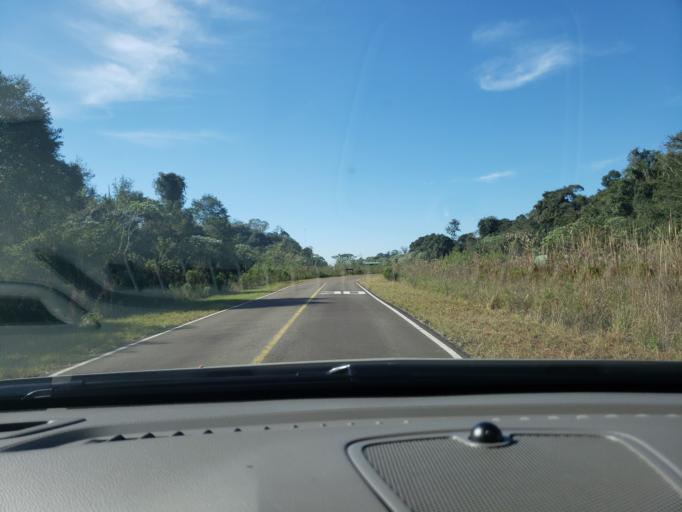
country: BR
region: Rio Grande do Sul
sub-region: Tres Passos
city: Tres Passos
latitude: -27.1521
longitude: -53.9081
